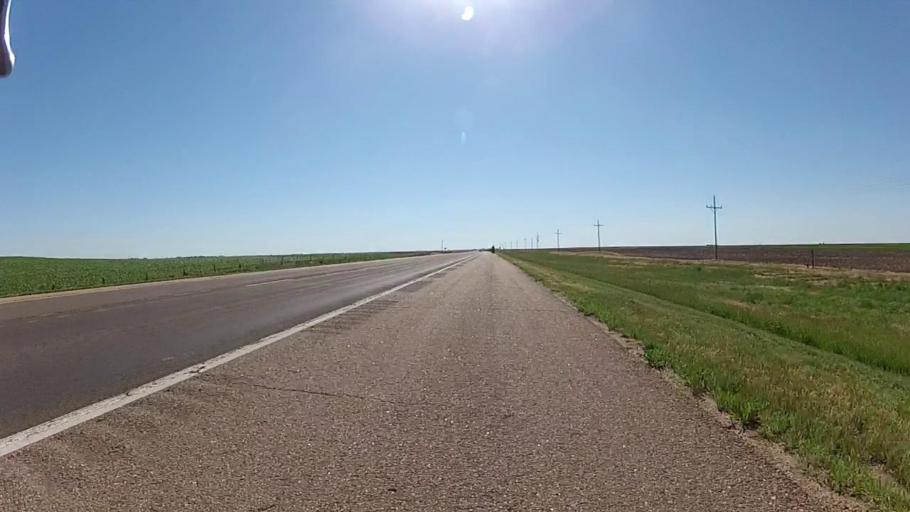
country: US
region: Kansas
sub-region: Kiowa County
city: Greensburg
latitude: 37.5862
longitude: -99.5543
